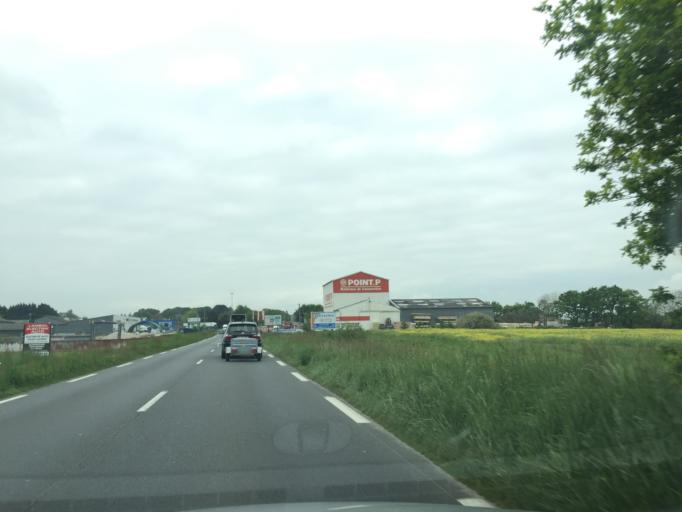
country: FR
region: Brittany
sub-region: Departement des Cotes-d'Armor
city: Lamballe
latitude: 48.4815
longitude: -2.4953
